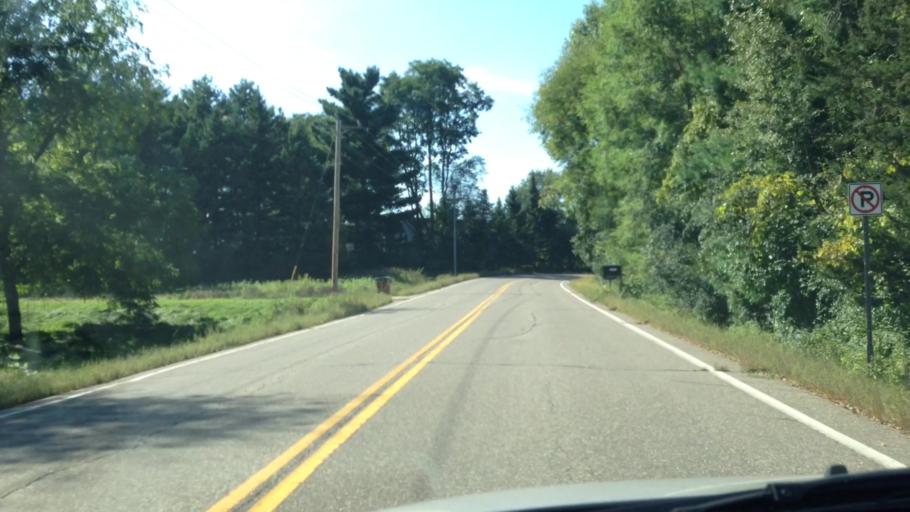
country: US
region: Minnesota
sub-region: Washington County
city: Stillwater
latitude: 45.0811
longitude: -92.8090
